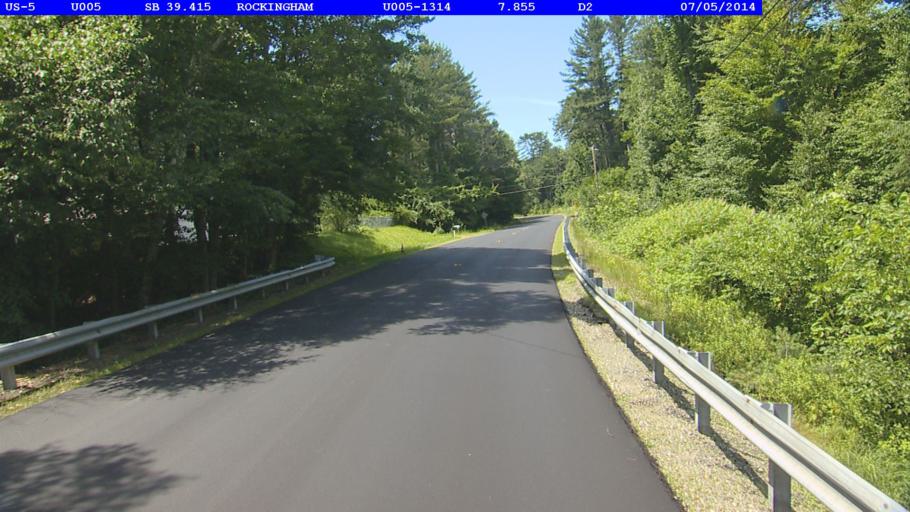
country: US
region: New Hampshire
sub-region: Sullivan County
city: Charlestown
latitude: 43.2229
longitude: -72.4466
